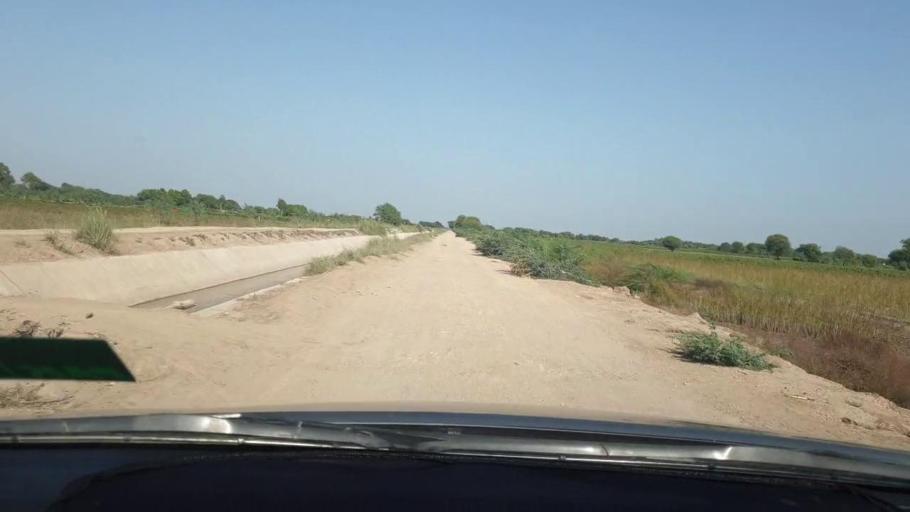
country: PK
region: Sindh
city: Naukot
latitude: 24.9302
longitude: 69.2666
